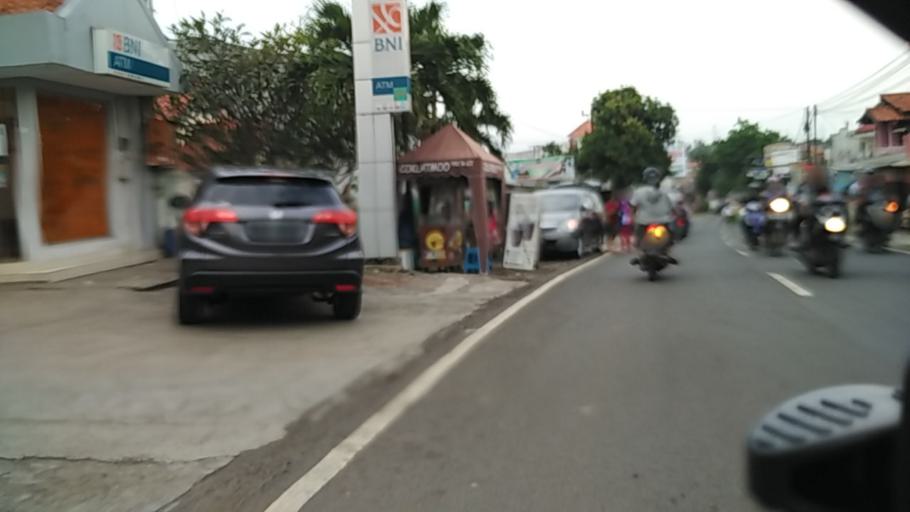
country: ID
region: Central Java
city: Semarang
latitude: -7.0564
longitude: 110.4291
